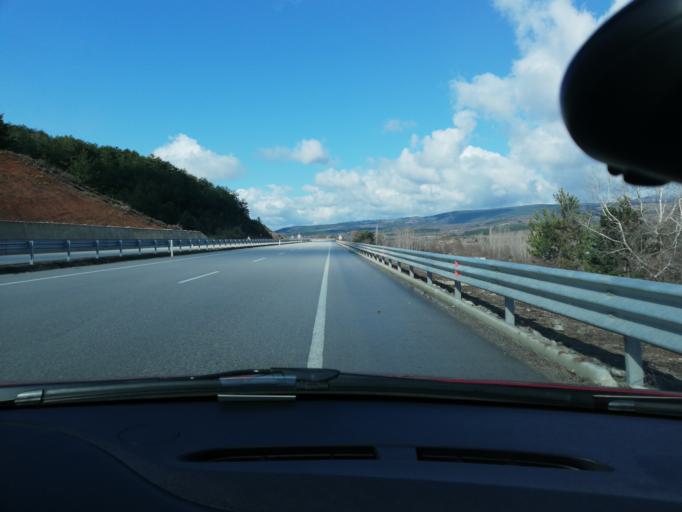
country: TR
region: Kastamonu
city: Arac
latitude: 41.2297
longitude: 33.2689
